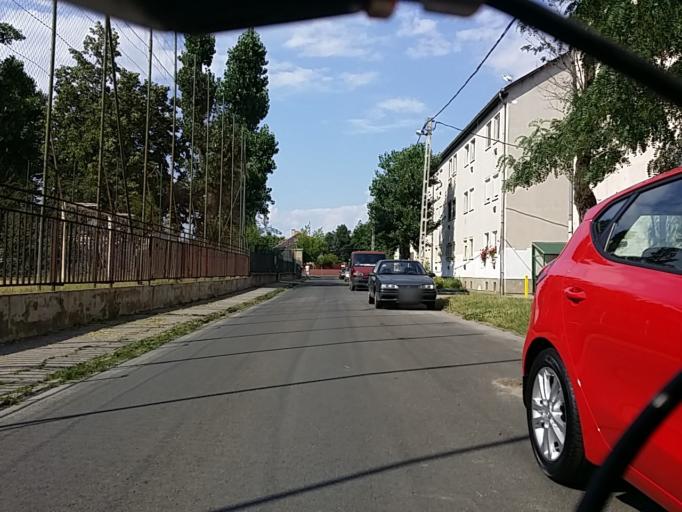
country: HU
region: Budapest
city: Budapest IV. keruelet
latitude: 47.5456
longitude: 19.0876
